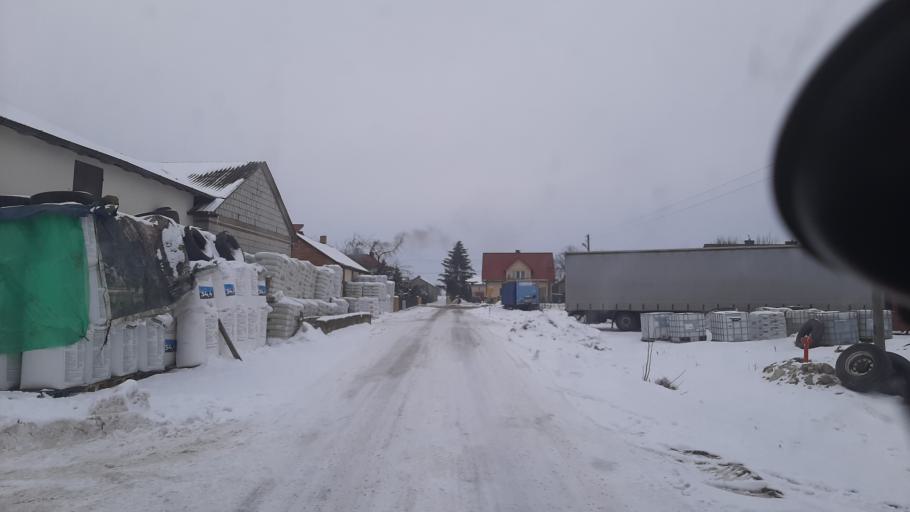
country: PL
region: Lublin Voivodeship
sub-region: Powiat lubelski
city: Garbow
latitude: 51.3587
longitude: 22.3760
